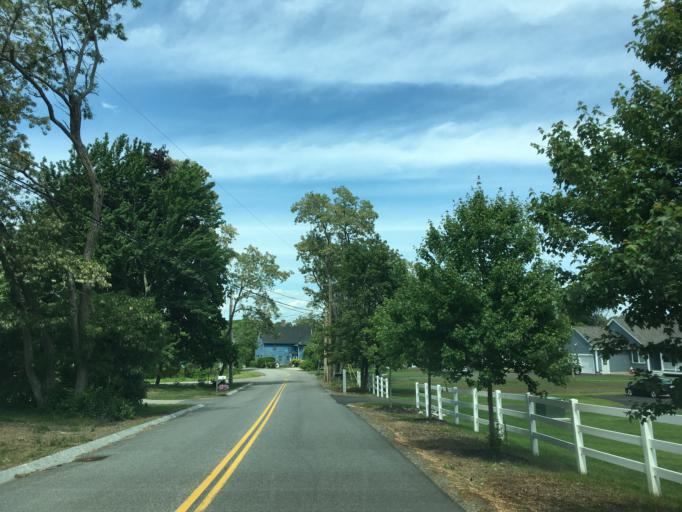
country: US
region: New Hampshire
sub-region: Rockingham County
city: Stratham Station
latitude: 43.0362
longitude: -70.8685
